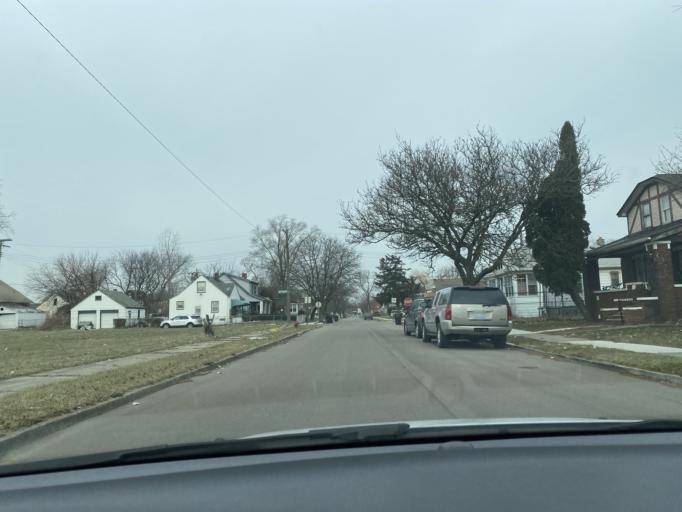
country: US
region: Michigan
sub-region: Wayne County
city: Highland Park
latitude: 42.3747
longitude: -83.1324
